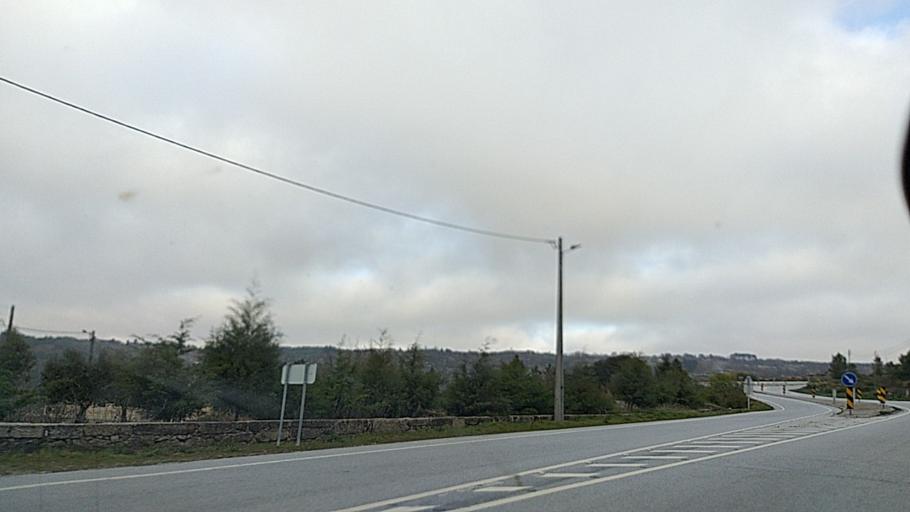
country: PT
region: Guarda
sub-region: Fornos de Algodres
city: Fornos de Algodres
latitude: 40.6570
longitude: -7.4846
